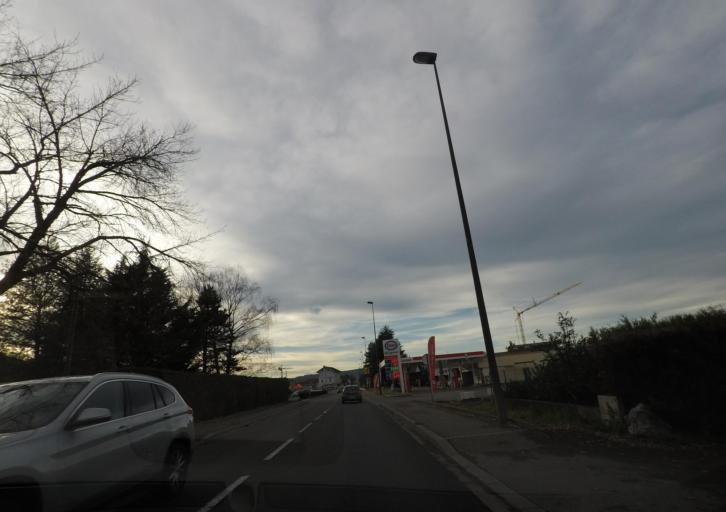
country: FR
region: Rhone-Alpes
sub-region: Departement de la Haute-Savoie
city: Bonneville
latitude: 46.0731
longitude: 6.3936
